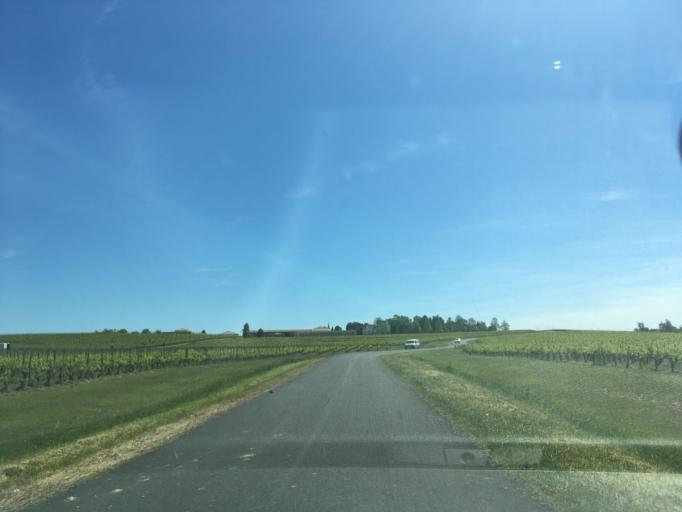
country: FR
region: Aquitaine
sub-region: Departement de la Gironde
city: Lesparre-Medoc
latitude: 45.3131
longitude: -0.8814
